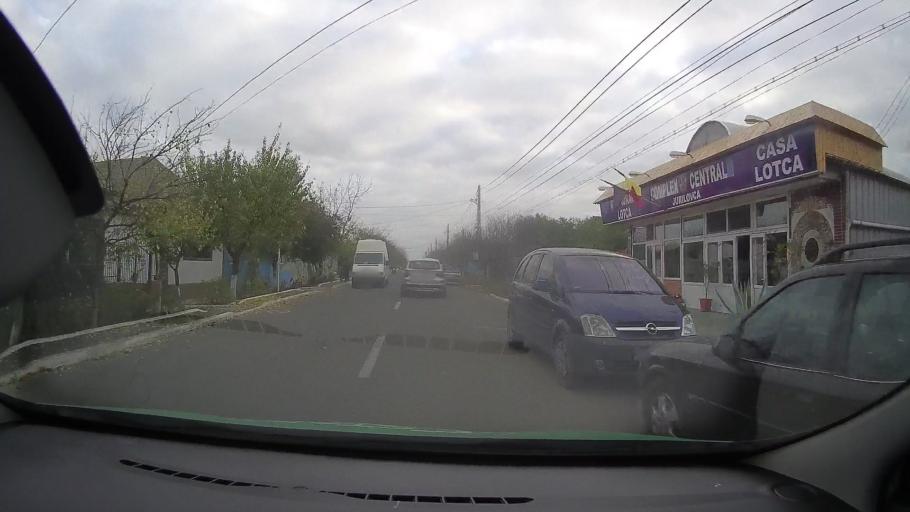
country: RO
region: Tulcea
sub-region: Comuna Jurilovca
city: Jurilovca
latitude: 44.7597
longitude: 28.8776
